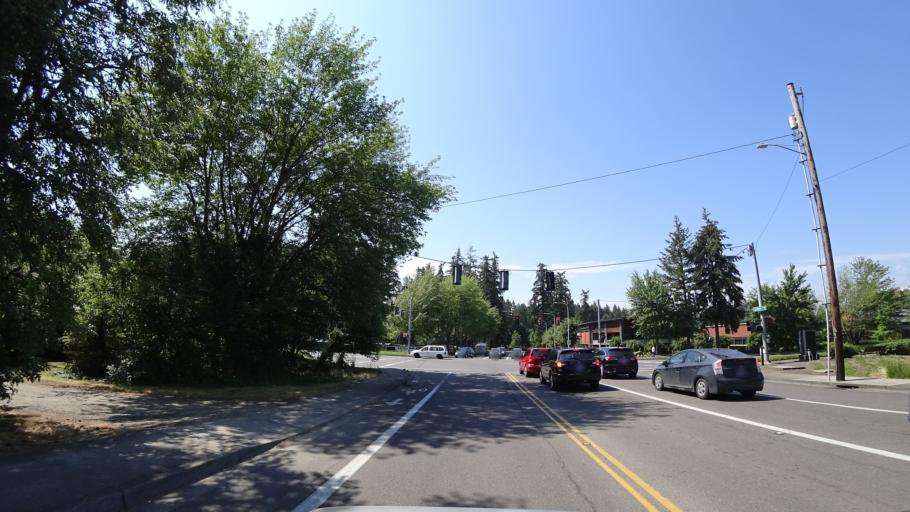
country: US
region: Oregon
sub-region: Washington County
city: Durham
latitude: 45.4187
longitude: -122.7239
